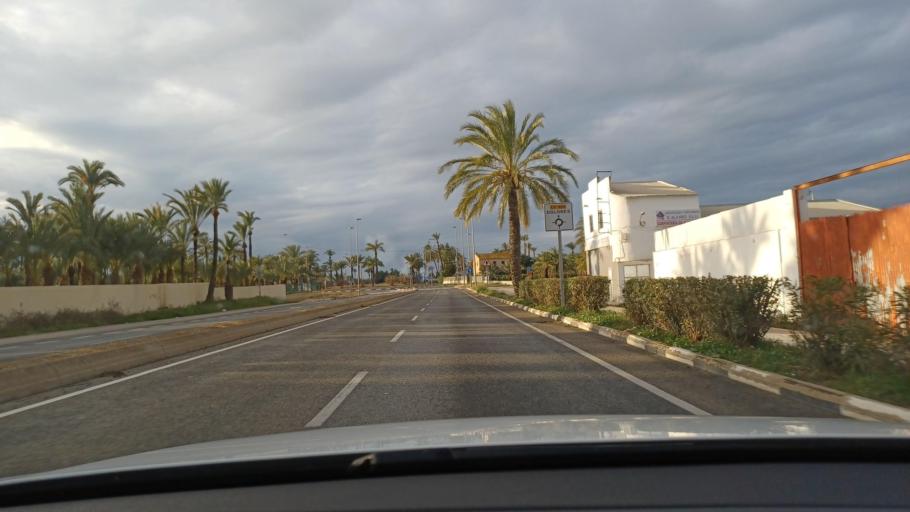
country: ES
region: Valencia
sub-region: Provincia de Alicante
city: Elche
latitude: 38.2446
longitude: -0.6992
